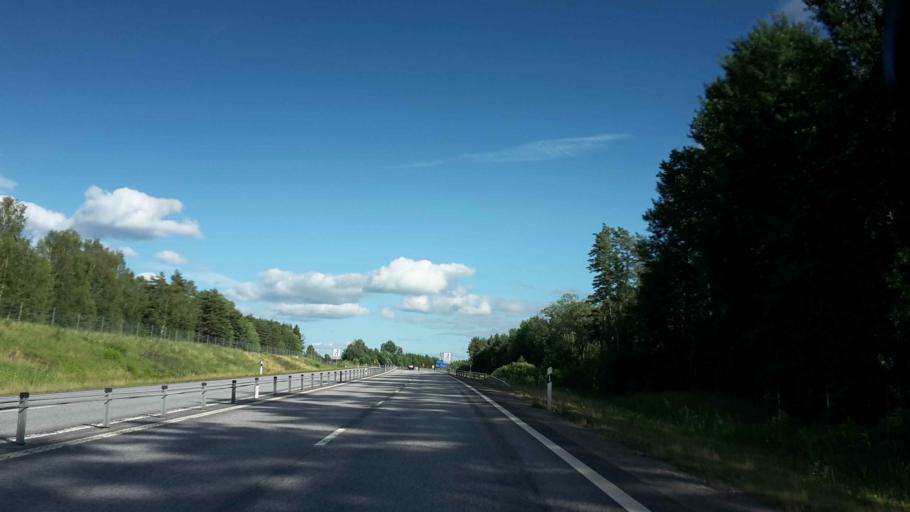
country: SE
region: OEstergoetland
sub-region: Norrkopings Kommun
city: Svartinge
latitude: 58.6406
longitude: 16.0900
